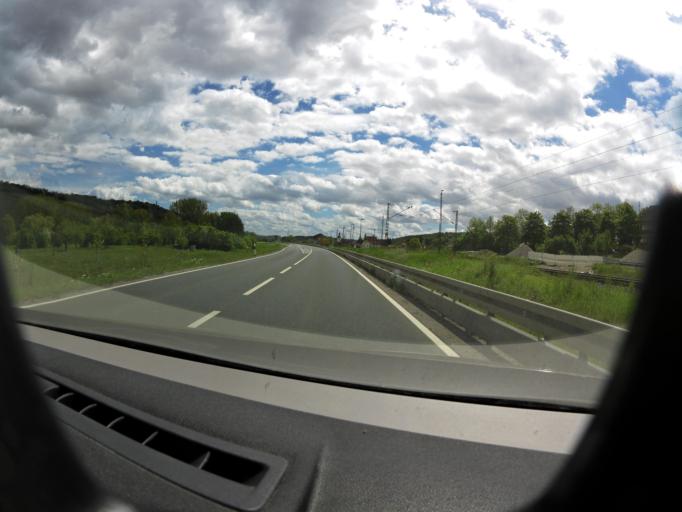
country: DE
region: Bavaria
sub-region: Regierungsbezirk Unterfranken
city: Sommerhausen
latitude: 49.6869
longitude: 10.0232
